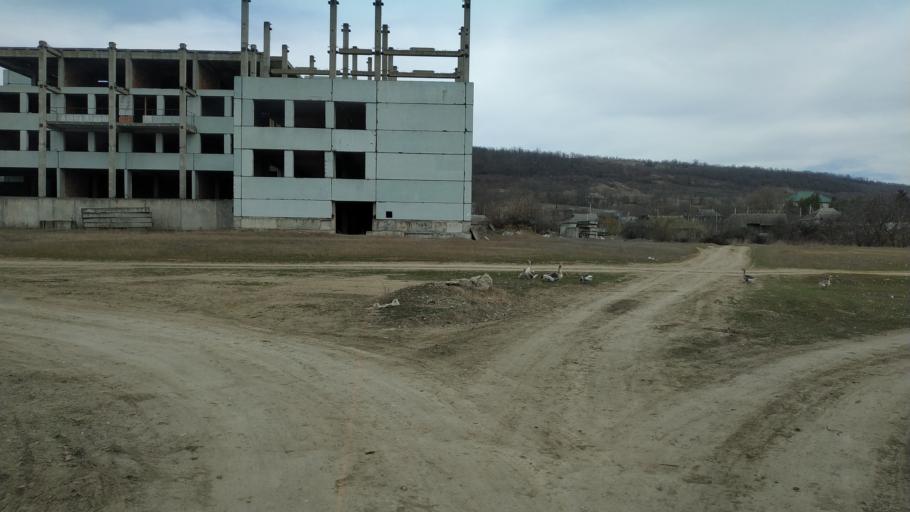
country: MD
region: Hincesti
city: Dancu
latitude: 46.9215
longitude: 28.2707
